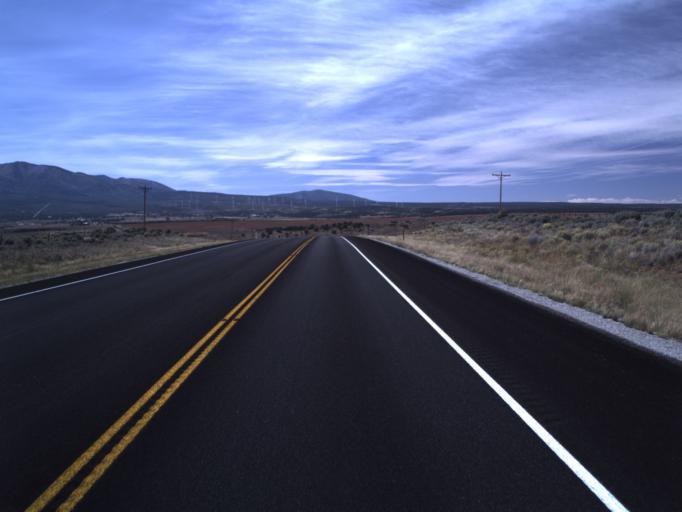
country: US
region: Utah
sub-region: San Juan County
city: Monticello
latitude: 37.8714
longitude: -109.2570
